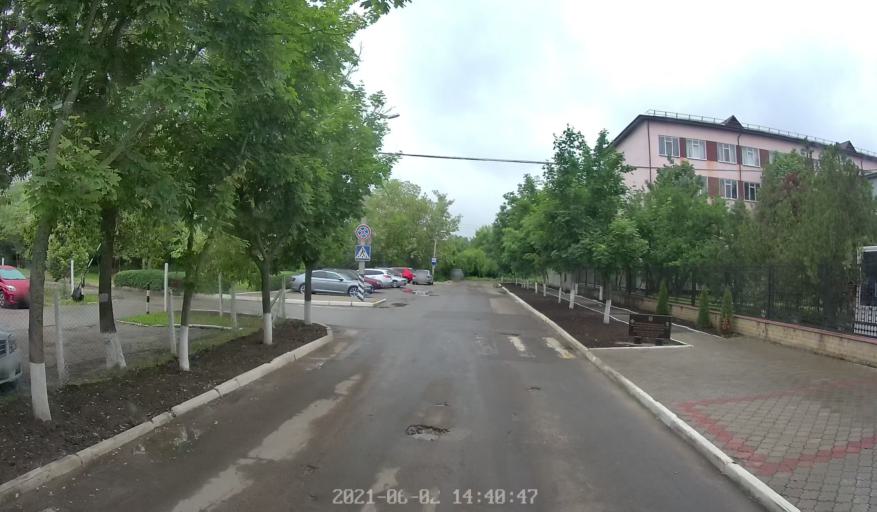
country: MD
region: Chisinau
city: Chisinau
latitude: 47.0465
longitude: 28.8009
